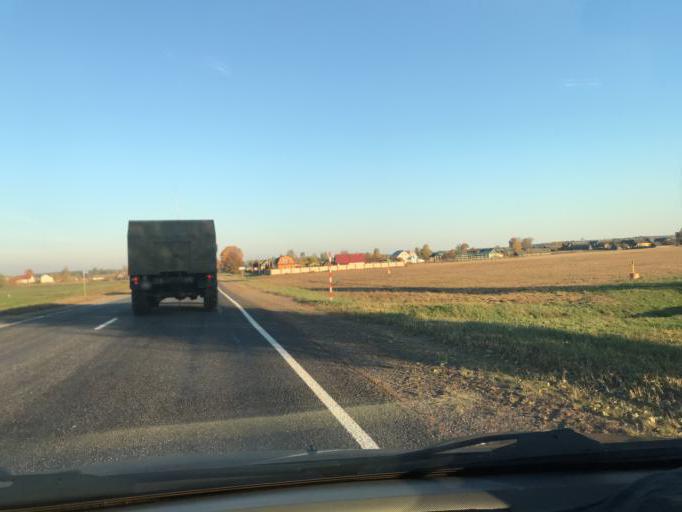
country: BY
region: Minsk
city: Staryya Darohi
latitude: 53.0469
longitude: 28.0989
